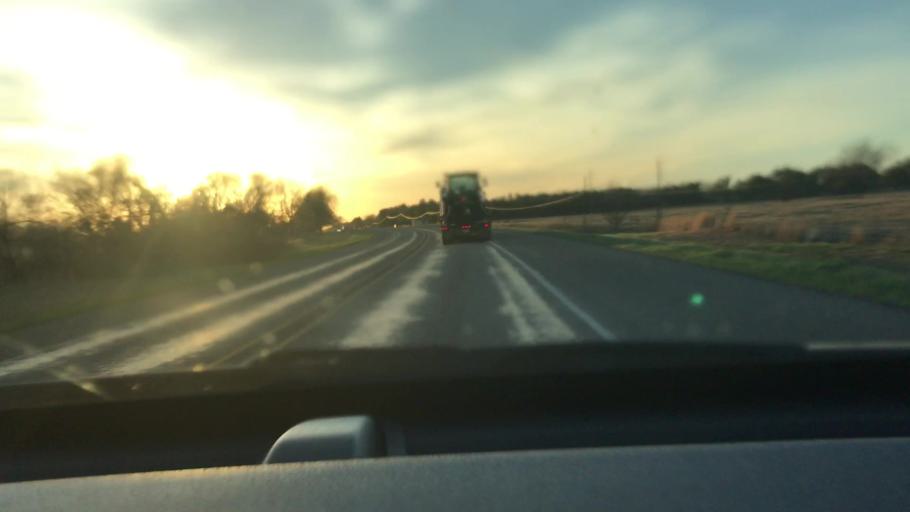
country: US
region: Texas
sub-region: Lamar County
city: Blossom
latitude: 33.6645
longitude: -95.3144
